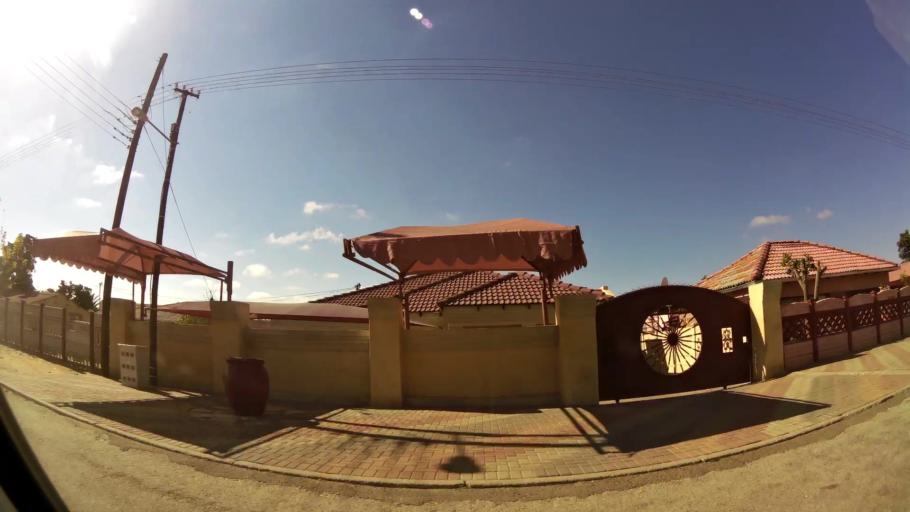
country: ZA
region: Limpopo
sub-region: Capricorn District Municipality
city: Polokwane
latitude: -23.8671
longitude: 29.3931
